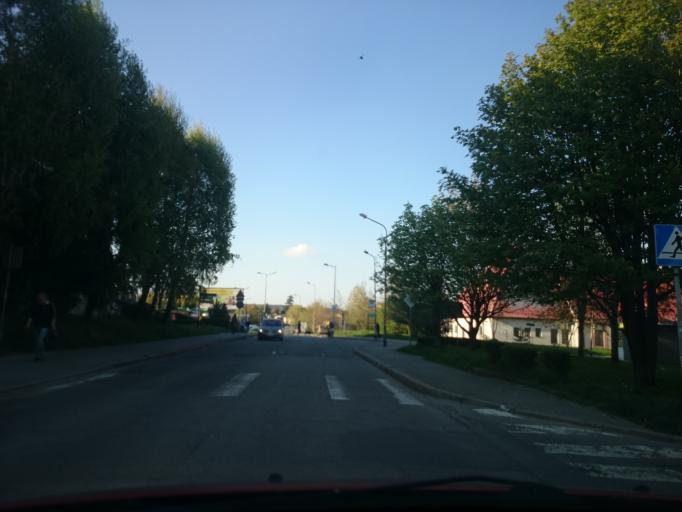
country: PL
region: Lower Silesian Voivodeship
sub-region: Powiat klodzki
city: Klodzko
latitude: 50.4368
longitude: 16.6414
